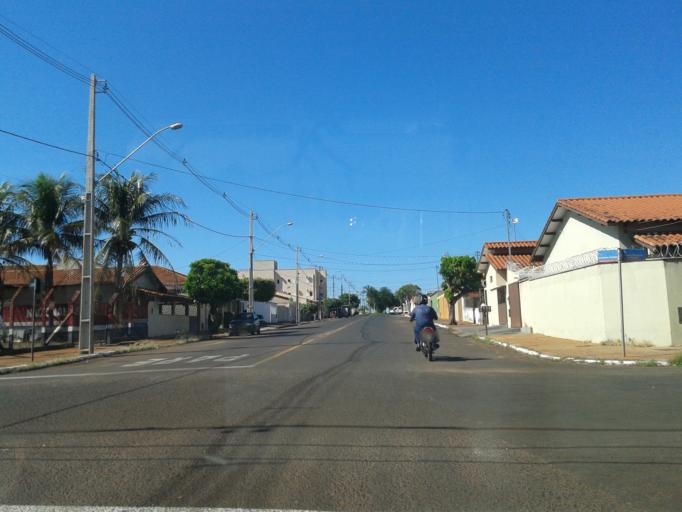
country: BR
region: Minas Gerais
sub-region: Santa Vitoria
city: Santa Vitoria
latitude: -18.8471
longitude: -50.1263
